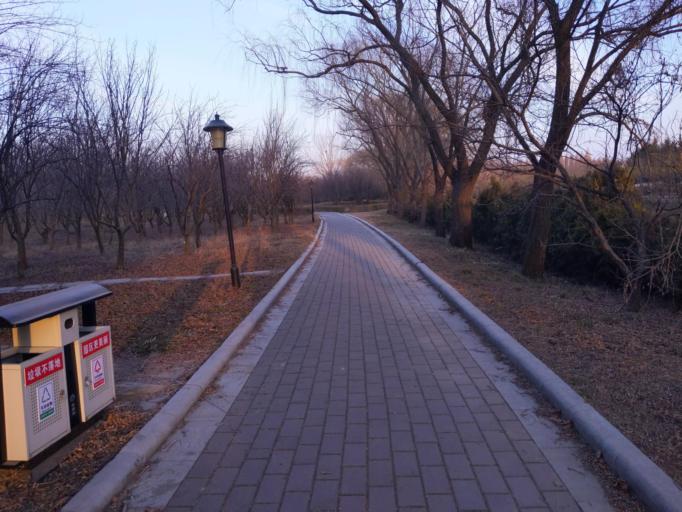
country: CN
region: Henan Sheng
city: Puyang
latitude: 35.7811
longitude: 114.9484
